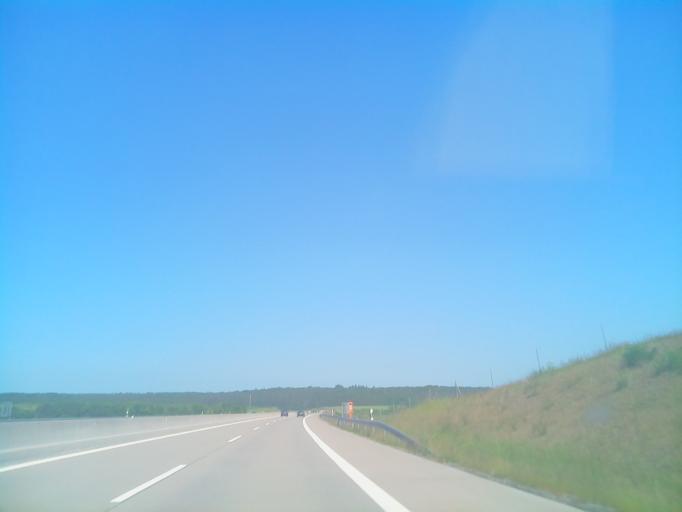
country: DE
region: Bavaria
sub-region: Regierungsbezirk Unterfranken
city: Strahlungen
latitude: 50.2698
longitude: 10.2348
